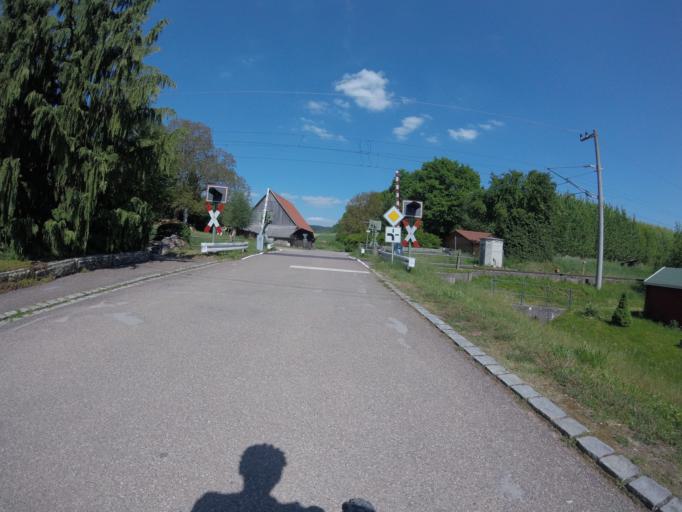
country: DE
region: Baden-Wuerttemberg
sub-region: Regierungsbezirk Stuttgart
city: Oppenweiler
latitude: 48.9728
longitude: 9.4622
